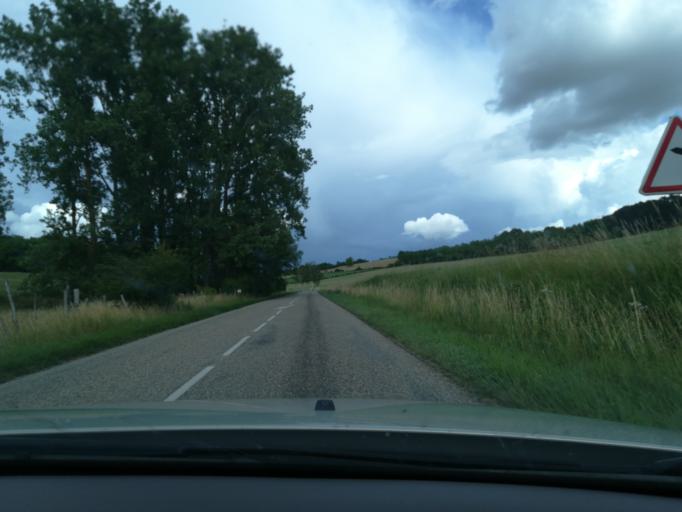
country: FR
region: Alsace
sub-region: Departement du Bas-Rhin
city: Bouxwiller
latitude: 48.8204
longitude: 7.4487
